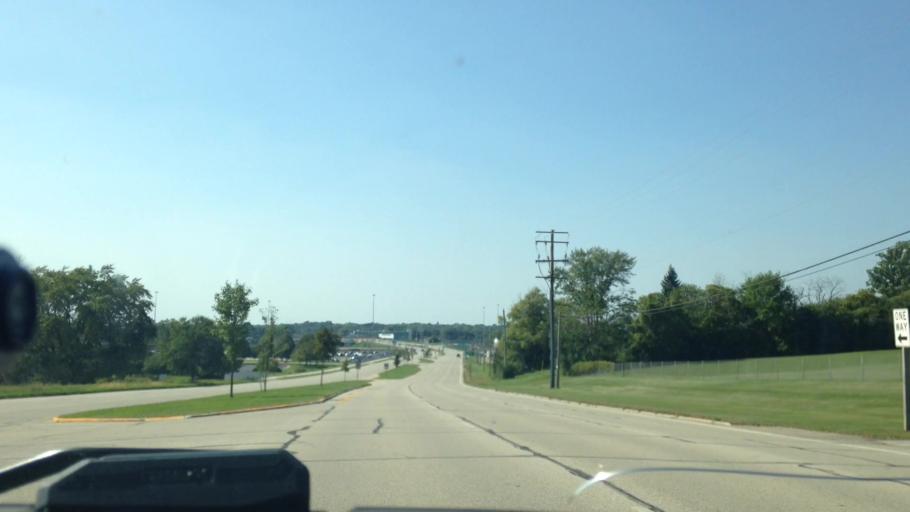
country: US
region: Wisconsin
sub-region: Waukesha County
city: Menomonee Falls
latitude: 43.1773
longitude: -88.0794
